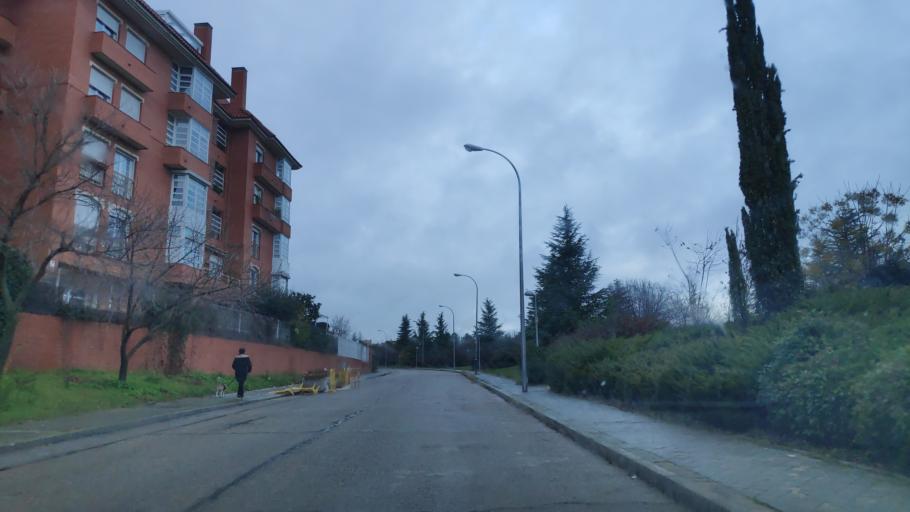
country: ES
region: Madrid
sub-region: Provincia de Madrid
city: San Blas
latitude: 40.4590
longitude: -3.6223
